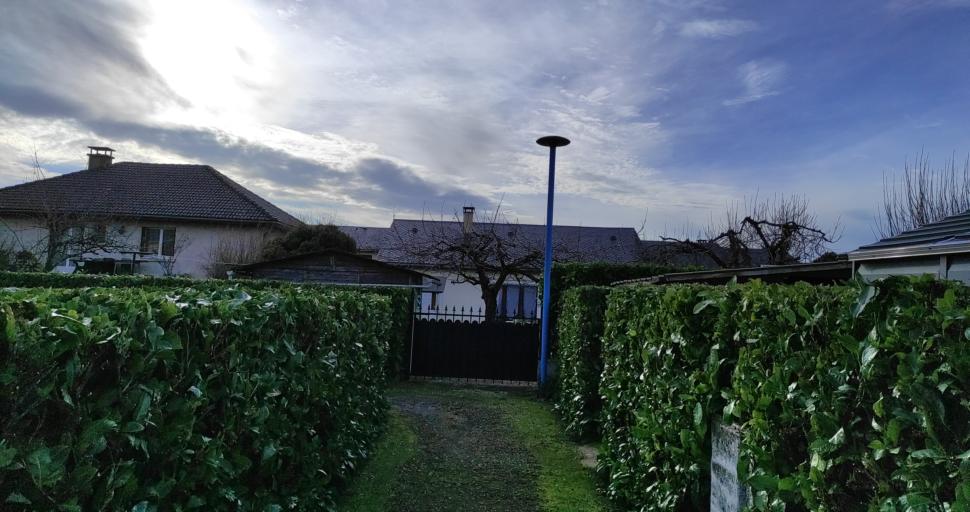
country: FR
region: Midi-Pyrenees
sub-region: Departement de l'Aveyron
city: Rodez
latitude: 44.3785
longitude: 2.5724
